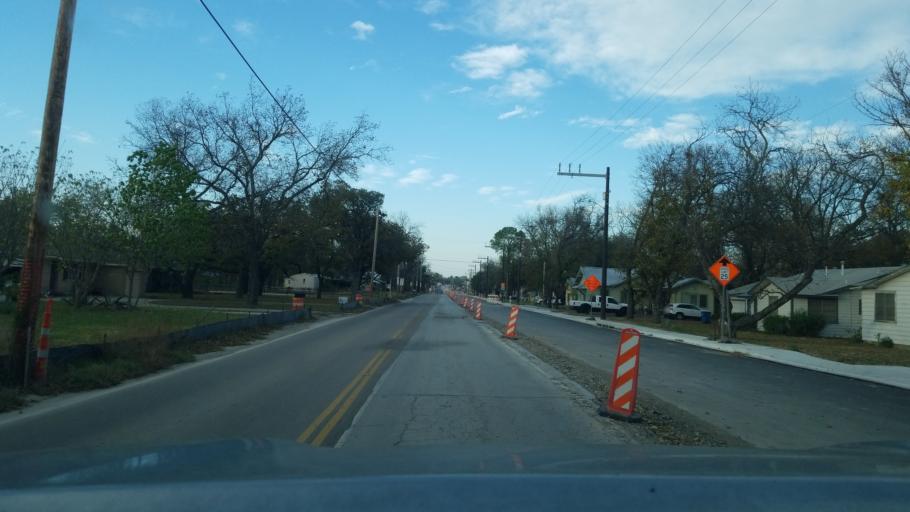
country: US
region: Texas
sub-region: Brown County
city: Lake Brownwood
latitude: 32.0912
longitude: -98.9640
